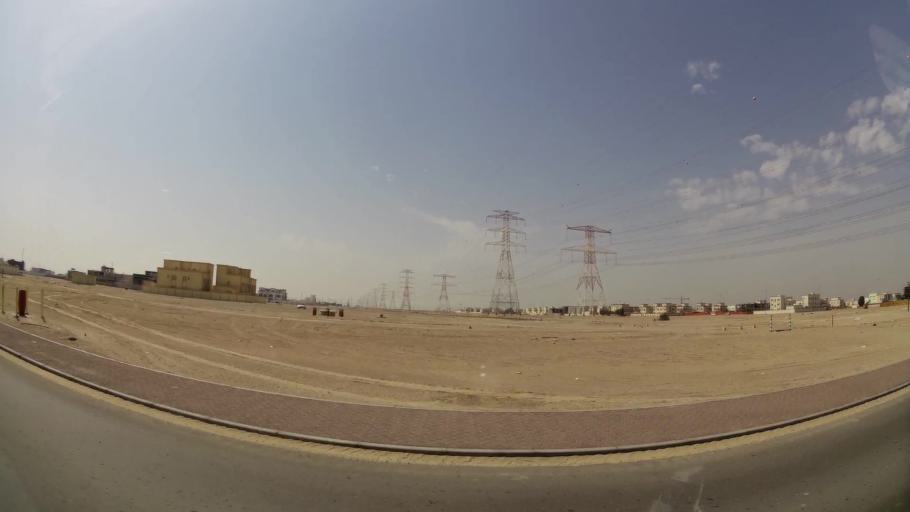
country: AE
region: Abu Dhabi
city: Abu Dhabi
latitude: 24.3062
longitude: 54.5751
